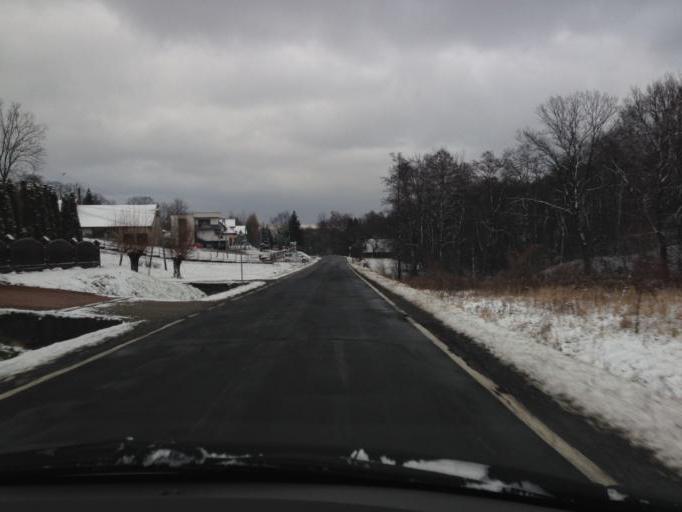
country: PL
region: Lesser Poland Voivodeship
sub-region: Powiat brzeski
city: Iwkowa
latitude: 49.8509
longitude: 20.6006
